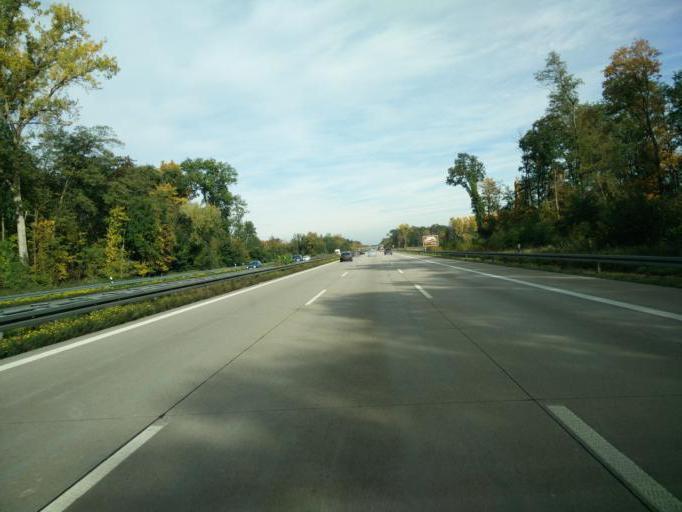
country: DE
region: Baden-Wuerttemberg
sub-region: Karlsruhe Region
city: Weingarten
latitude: 49.0488
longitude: 8.4934
